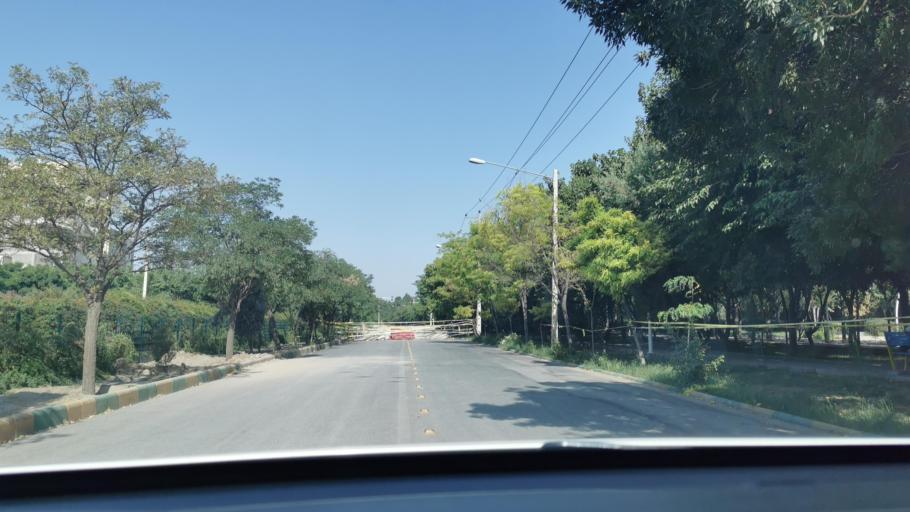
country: IR
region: Razavi Khorasan
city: Mashhad
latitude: 36.3306
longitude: 59.6324
